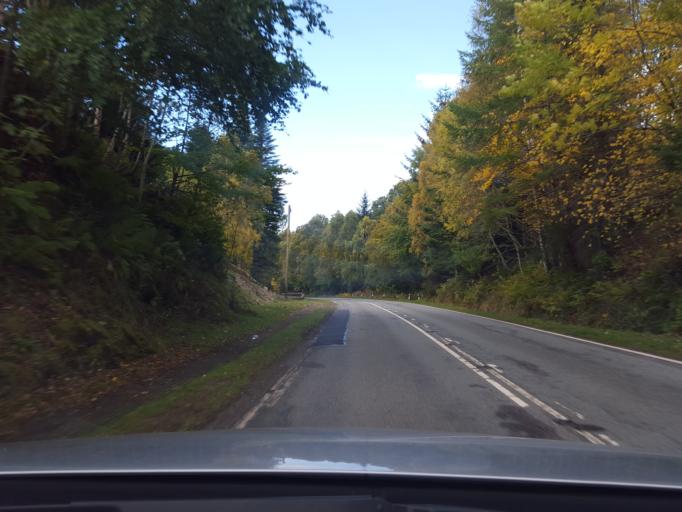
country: GB
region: Scotland
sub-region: Highland
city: Fort William
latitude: 57.2393
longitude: -5.4456
